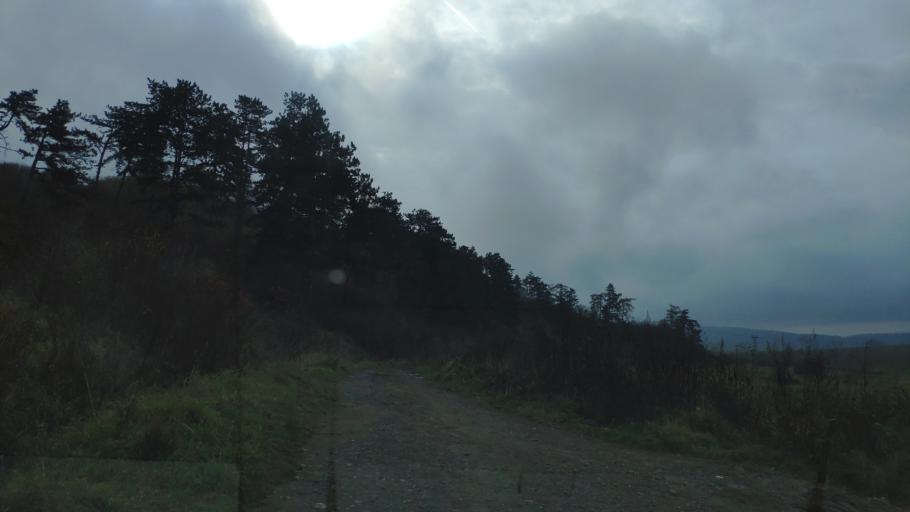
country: SK
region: Presovsky
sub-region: Okres Presov
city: Presov
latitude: 49.0270
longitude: 21.1999
